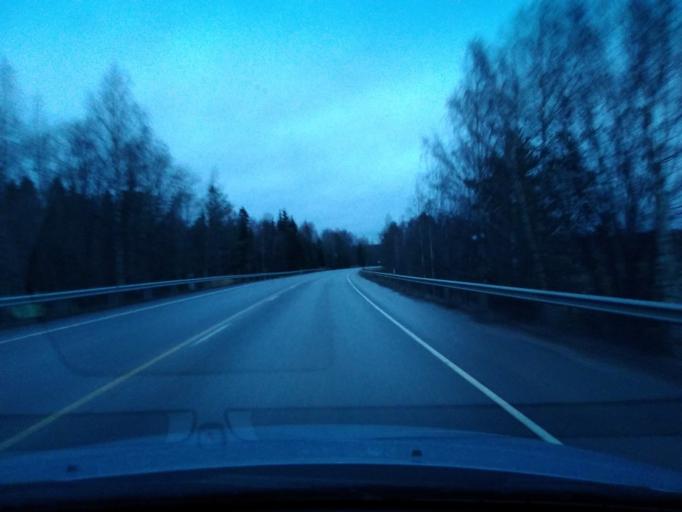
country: FI
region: Uusimaa
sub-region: Porvoo
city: Porvoo
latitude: 60.4084
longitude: 25.5846
